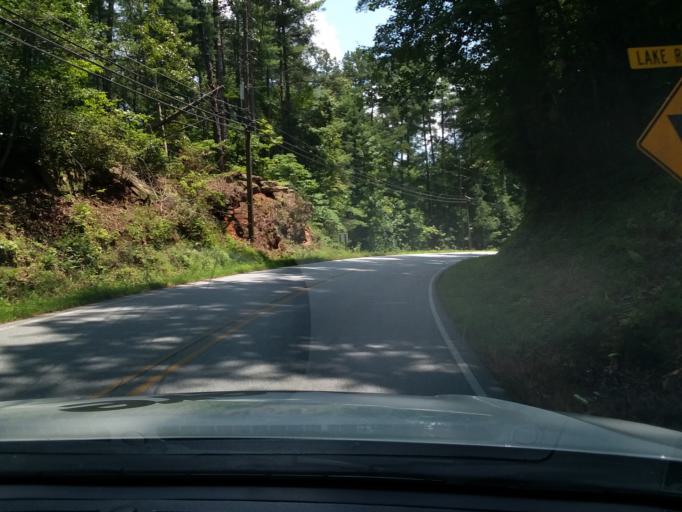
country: US
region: Georgia
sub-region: Rabun County
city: Clayton
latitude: 34.7812
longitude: -83.4163
